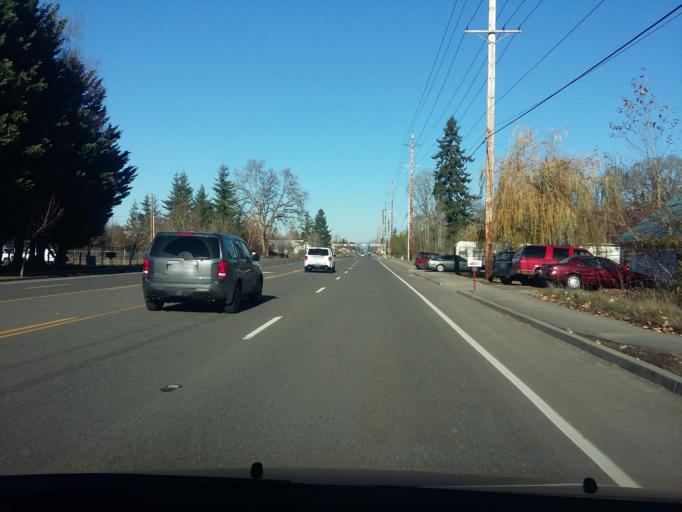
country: US
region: Washington
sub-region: Clark County
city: Barberton
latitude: 45.6902
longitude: -122.5992
